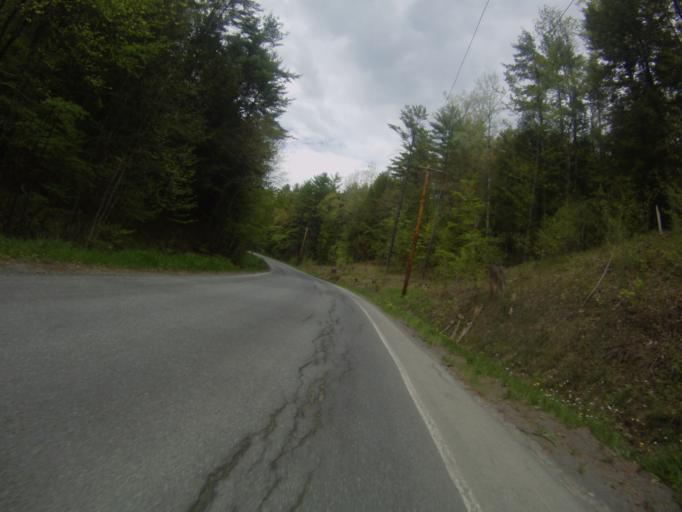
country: US
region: New York
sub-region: Essex County
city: Port Henry
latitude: 43.9465
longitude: -73.4714
